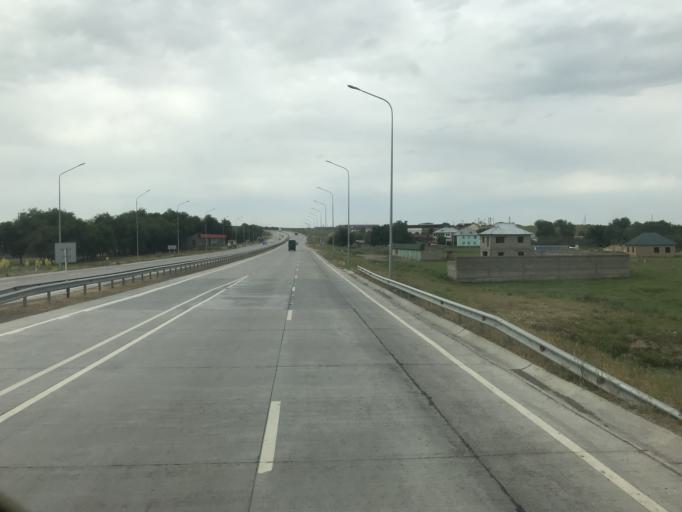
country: KZ
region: Ongtustik Qazaqstan
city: Shymkent
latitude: 42.2125
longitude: 69.5207
